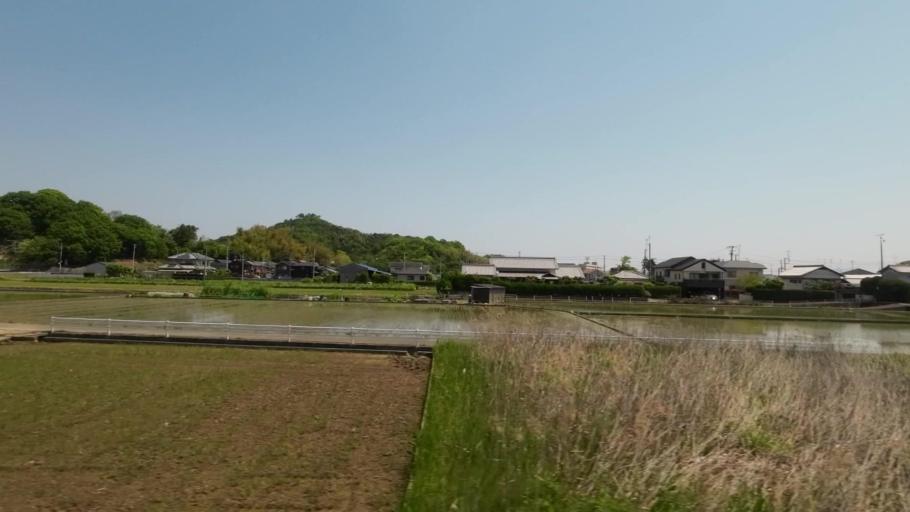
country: JP
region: Ehime
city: Saijo
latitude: 34.0203
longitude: 133.0280
